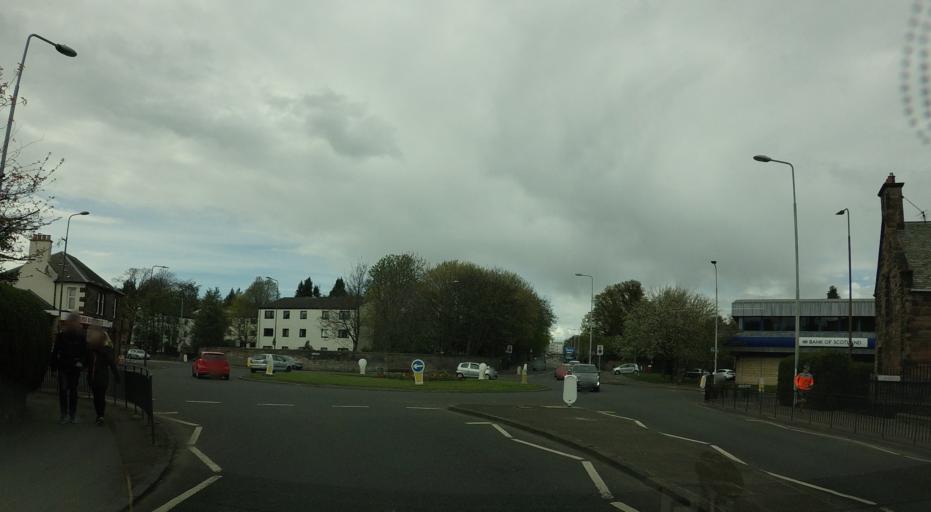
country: GB
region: Scotland
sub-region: Edinburgh
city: Edinburgh
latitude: 55.9584
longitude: -3.2261
